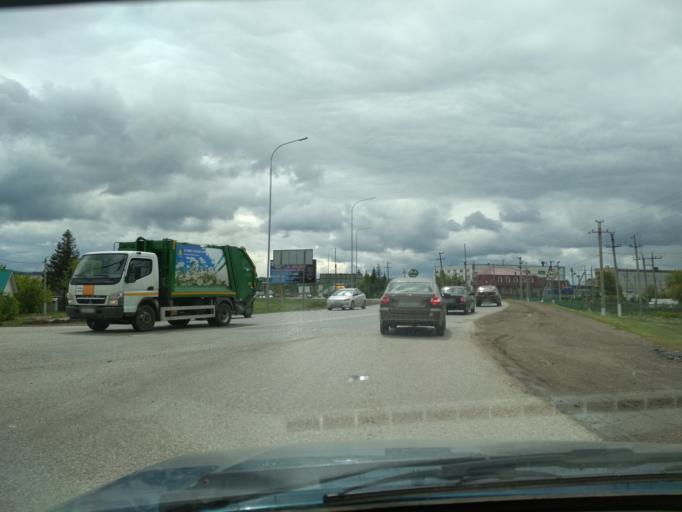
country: RU
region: Tatarstan
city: Zainsk
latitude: 55.3037
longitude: 52.0051
